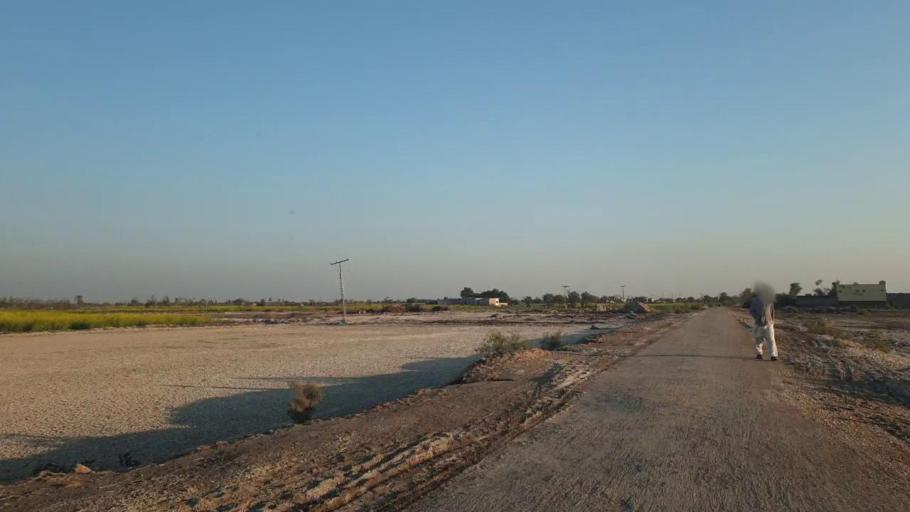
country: PK
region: Sindh
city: Khadro
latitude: 26.0794
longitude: 68.6869
